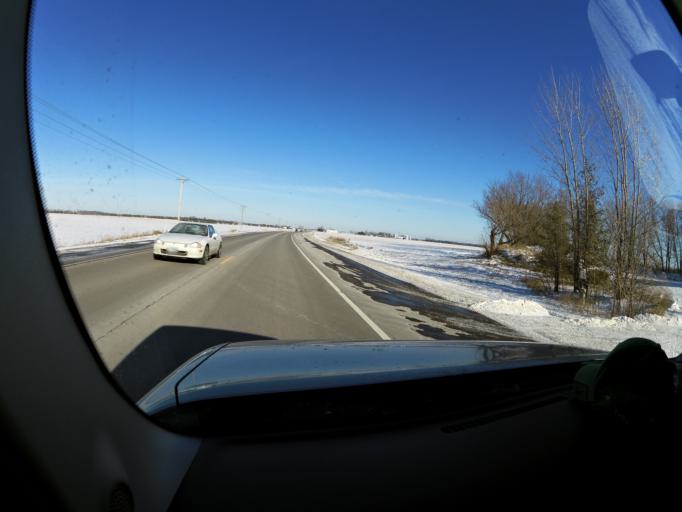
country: US
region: Minnesota
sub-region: Dakota County
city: Hastings
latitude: 44.6950
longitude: -92.9025
